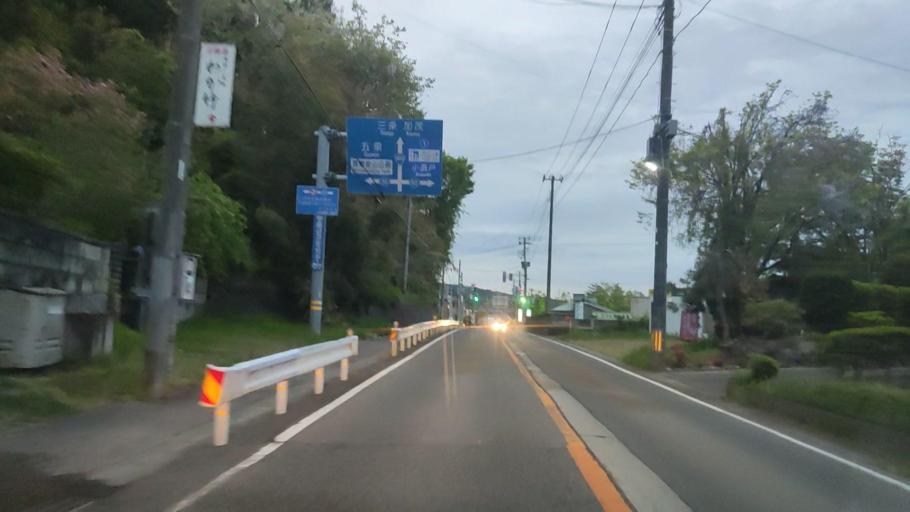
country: JP
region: Niigata
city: Kamo
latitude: 37.7140
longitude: 139.0735
